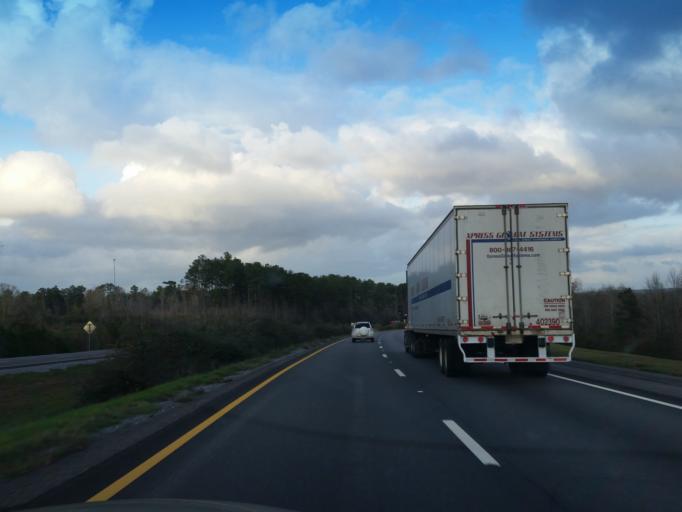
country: US
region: Mississippi
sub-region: Jones County
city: Sharon
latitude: 31.8994
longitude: -89.0273
